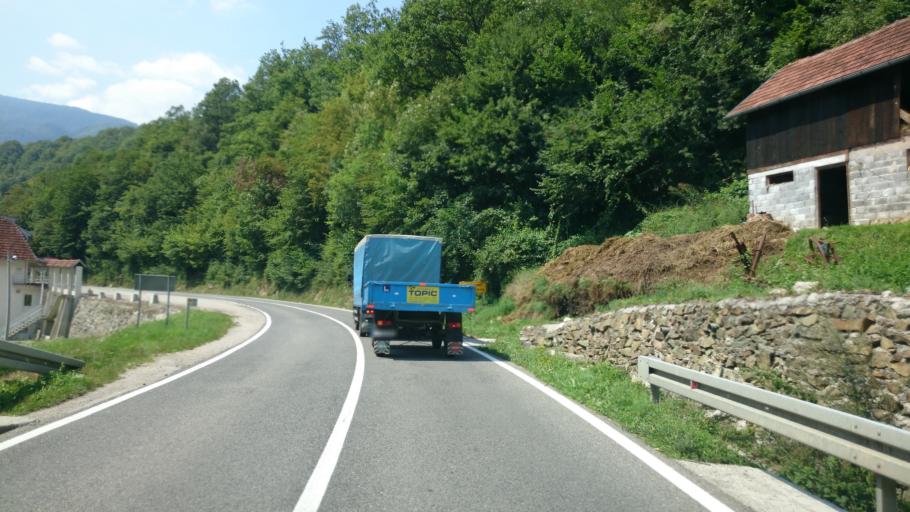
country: BA
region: Federation of Bosnia and Herzegovina
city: Jajce
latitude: 44.2328
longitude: 17.3134
